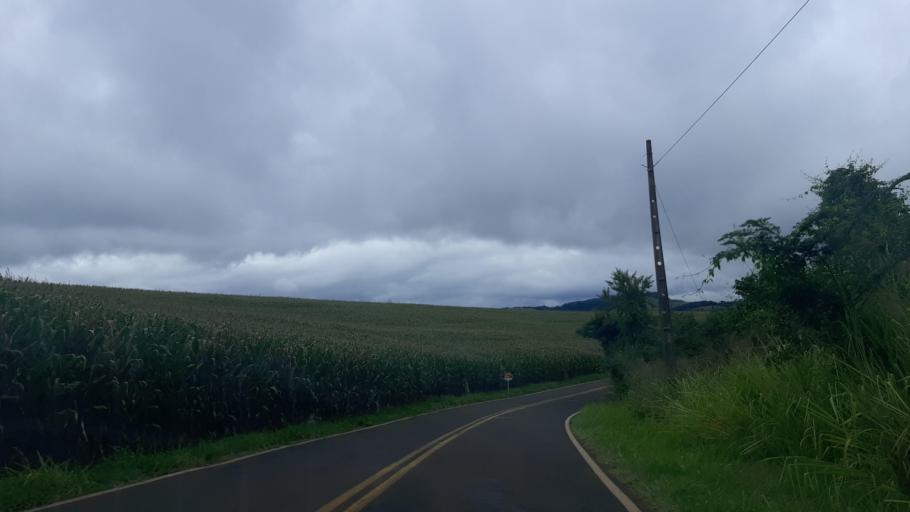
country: BR
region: Parana
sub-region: Ampere
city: Ampere
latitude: -25.9882
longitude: -53.4394
